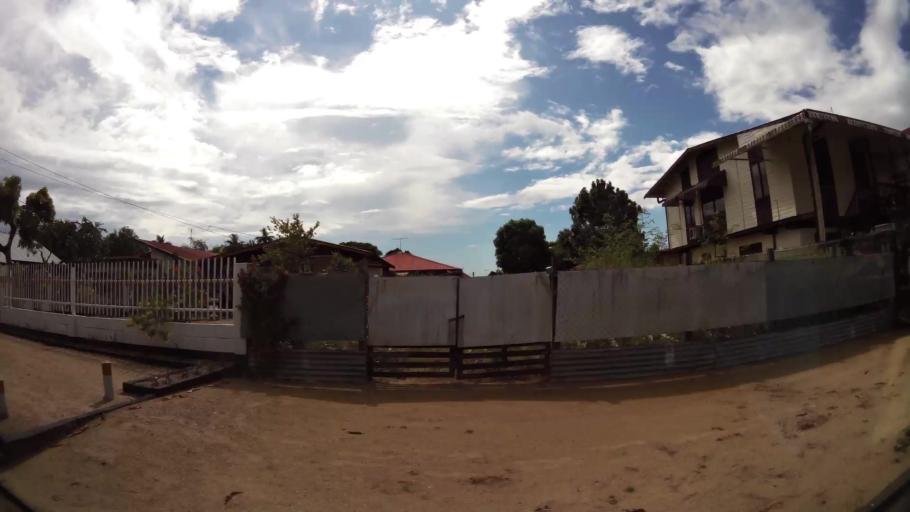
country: SR
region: Paramaribo
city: Paramaribo
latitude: 5.8392
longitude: -55.1488
